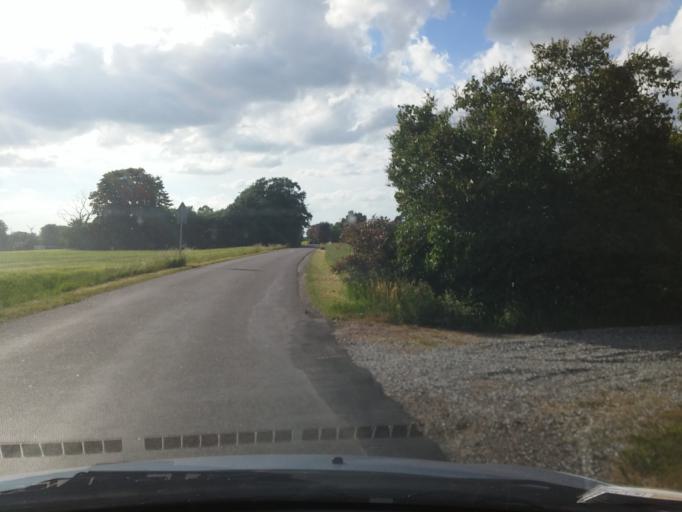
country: DK
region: South Denmark
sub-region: Kerteminde Kommune
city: Langeskov
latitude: 55.3941
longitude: 10.5595
